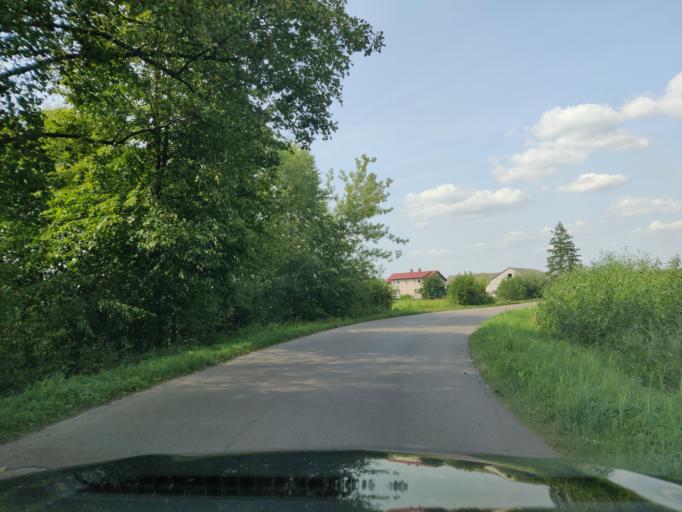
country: PL
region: Masovian Voivodeship
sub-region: Powiat wyszkowski
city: Rzasnik
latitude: 52.7440
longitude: 21.3180
